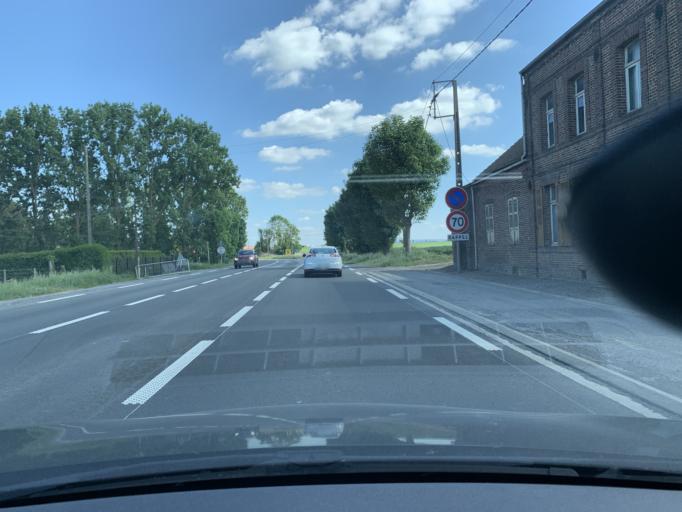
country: FR
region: Nord-Pas-de-Calais
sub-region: Departement du Nord
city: Raillencourt-Sainte-Olle
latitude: 50.2119
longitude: 3.1866
